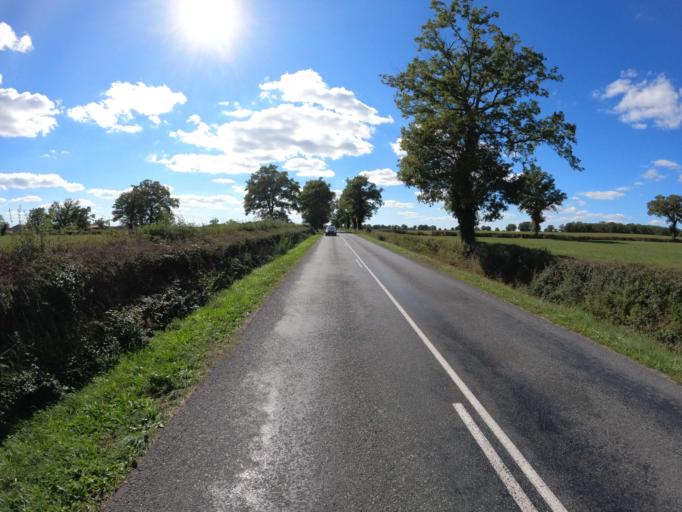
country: FR
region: Auvergne
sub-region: Departement de l'Allier
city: Doyet
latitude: 46.3895
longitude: 2.8047
